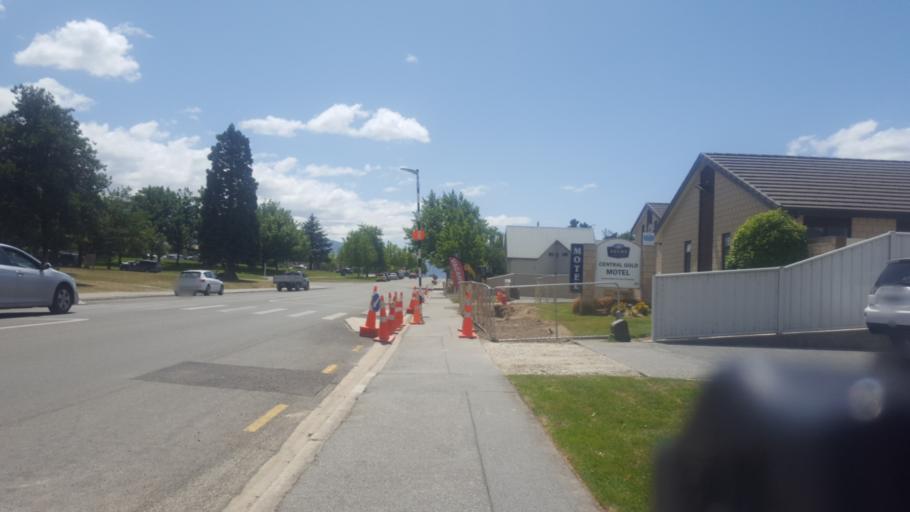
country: NZ
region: Otago
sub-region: Queenstown-Lakes District
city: Wanaka
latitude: -45.0392
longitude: 169.1982
